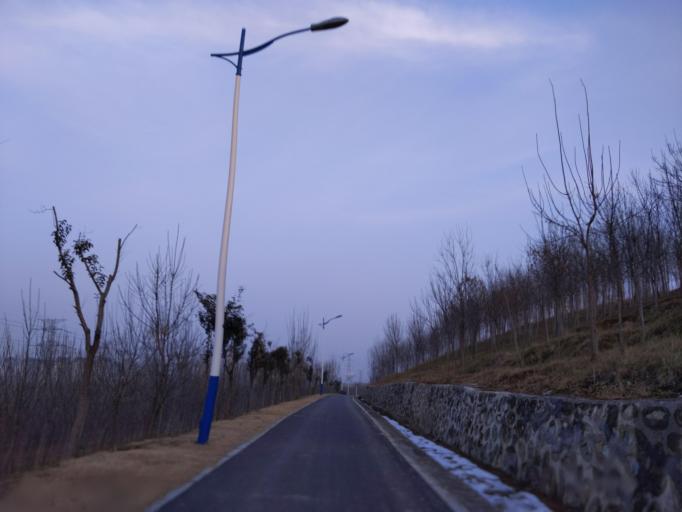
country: CN
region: Henan Sheng
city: Zhongyuanlu
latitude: 35.8189
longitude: 115.0470
